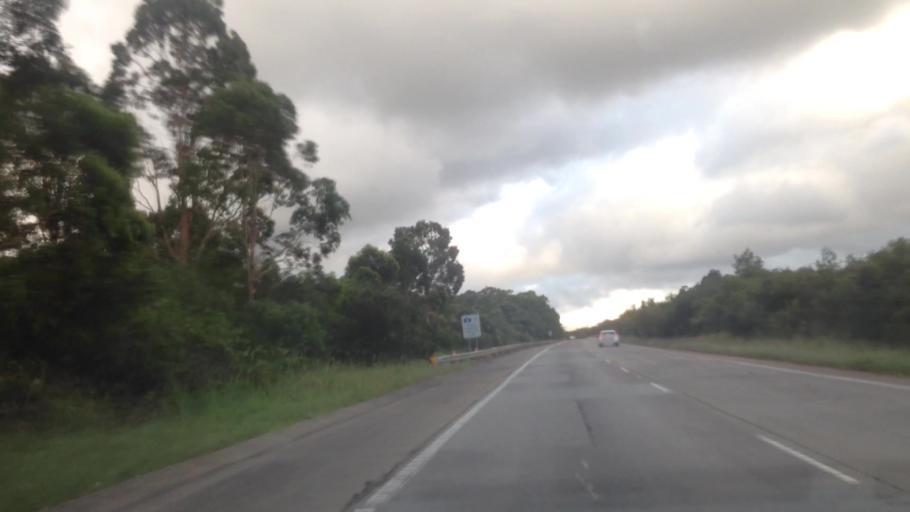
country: AU
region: New South Wales
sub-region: Wyong Shire
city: Jilliby
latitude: -33.2070
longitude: 151.4557
